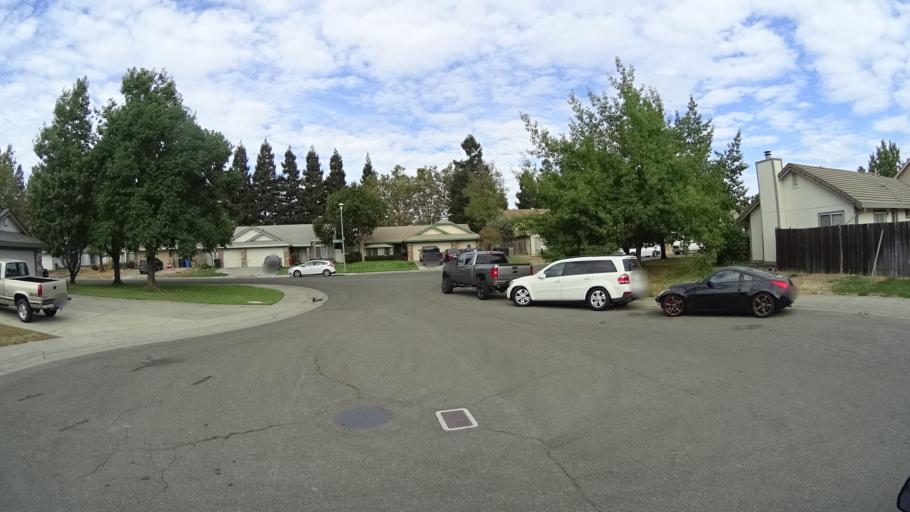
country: US
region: California
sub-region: Sacramento County
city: Laguna
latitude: 38.4464
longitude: -121.4244
